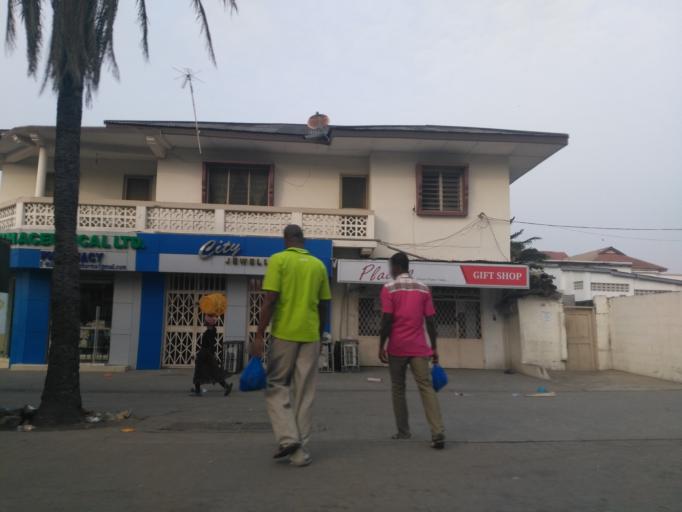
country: GH
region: Greater Accra
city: Accra
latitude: 5.5632
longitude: -0.2138
